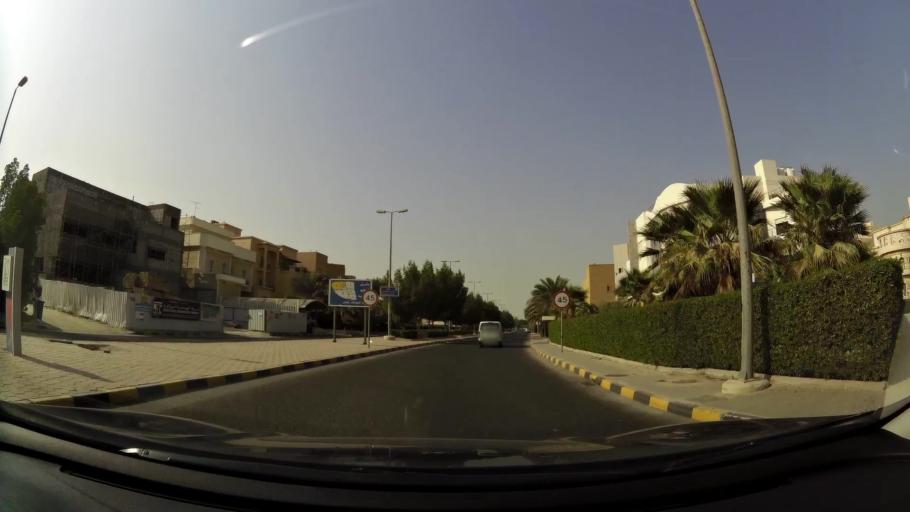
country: KW
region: Mubarak al Kabir
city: Sabah as Salim
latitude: 29.2777
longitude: 48.0435
